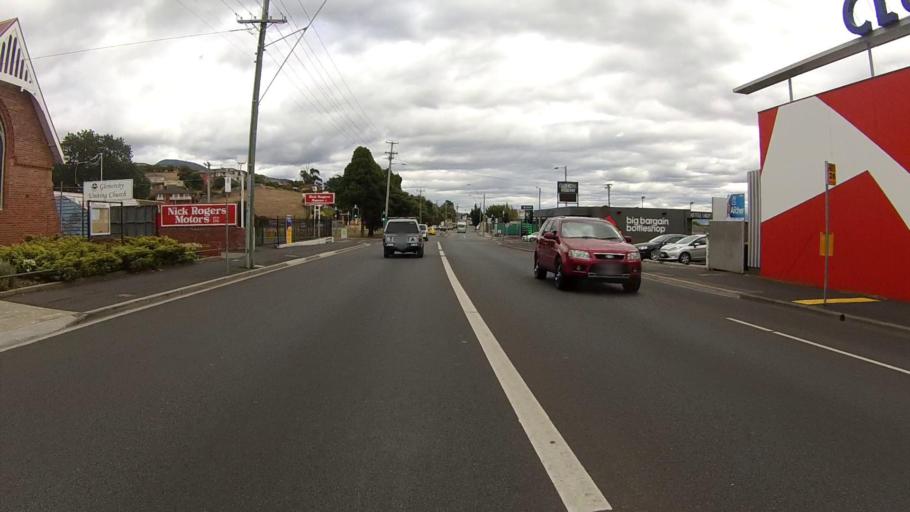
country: AU
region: Tasmania
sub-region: Glenorchy
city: Glenorchy
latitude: -42.8304
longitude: 147.2696
